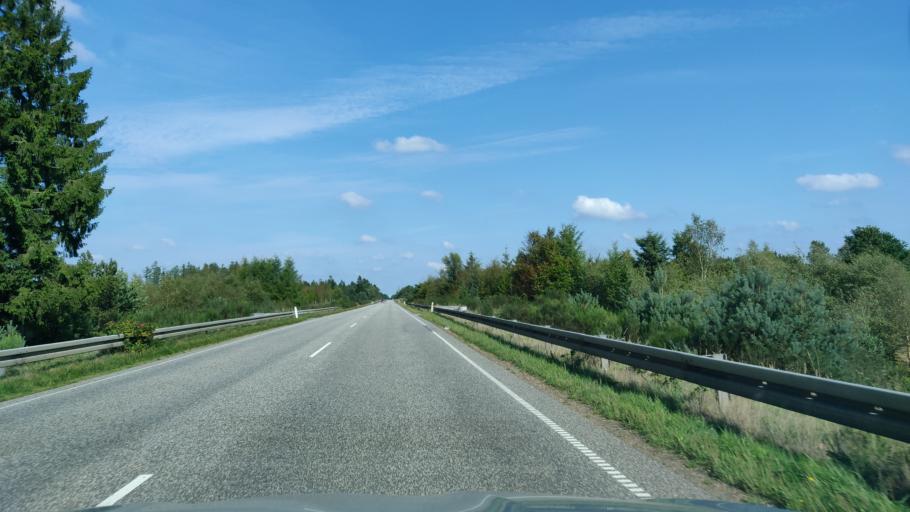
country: DK
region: Central Jutland
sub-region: Herning Kommune
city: Sunds
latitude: 56.3652
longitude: 8.9783
